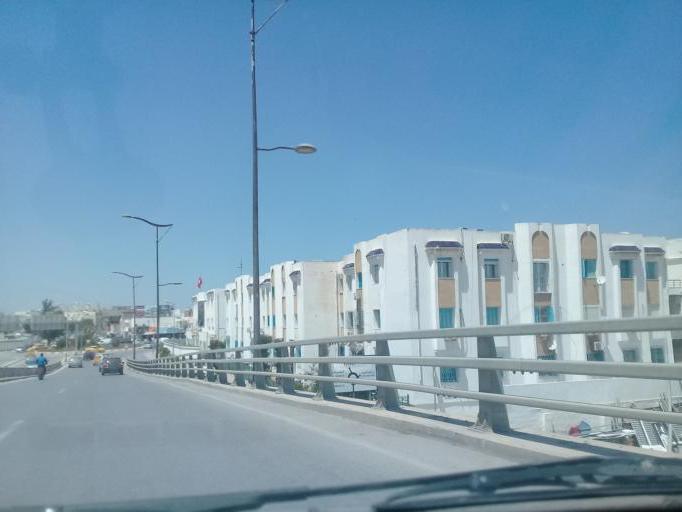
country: TN
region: Tunis
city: La Goulette
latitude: 36.8484
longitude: 10.2604
